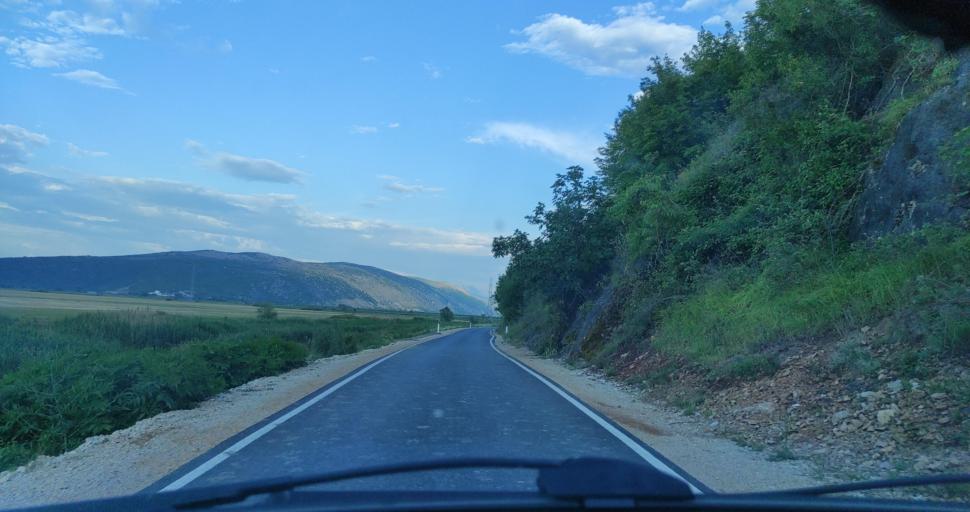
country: AL
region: Shkoder
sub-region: Rrethi i Shkodres
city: Velipoje
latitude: 41.9296
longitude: 19.4432
